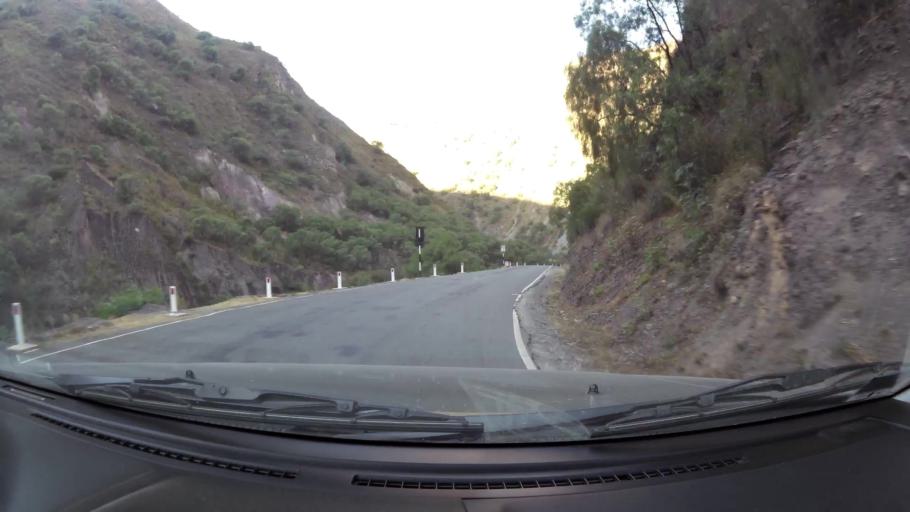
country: PE
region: Huancavelica
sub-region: Provincia de Churcampa
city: La Esmeralda
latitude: -12.5493
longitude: -74.7032
